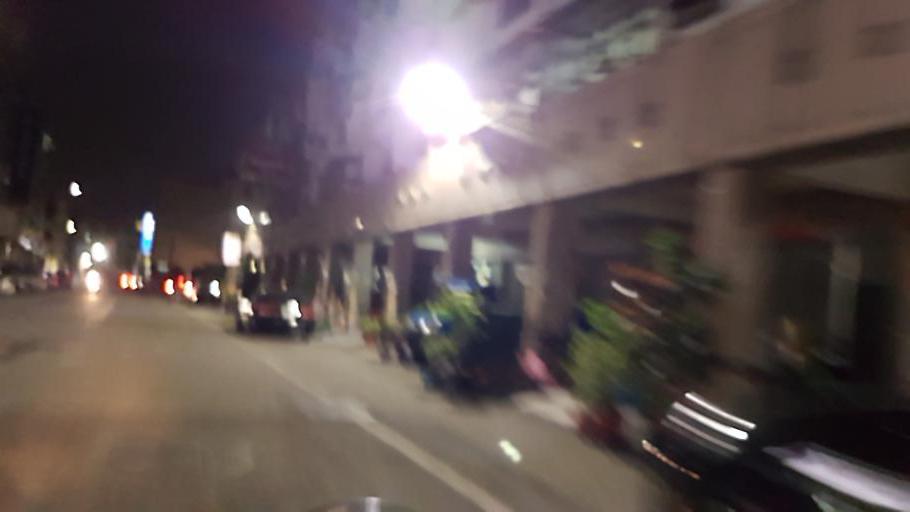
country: TW
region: Taiwan
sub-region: Changhua
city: Chang-hua
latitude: 24.0634
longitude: 120.5253
